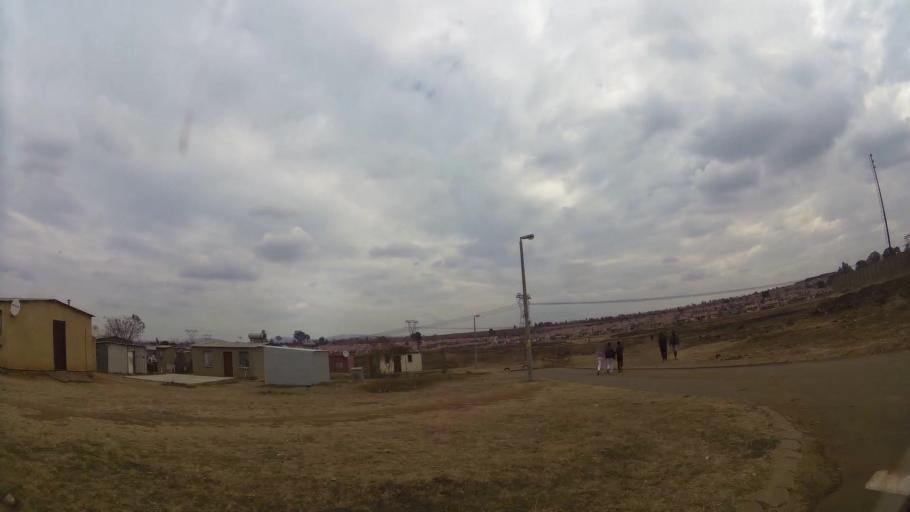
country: ZA
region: Gauteng
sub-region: Ekurhuleni Metropolitan Municipality
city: Germiston
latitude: -26.3708
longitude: 28.1197
